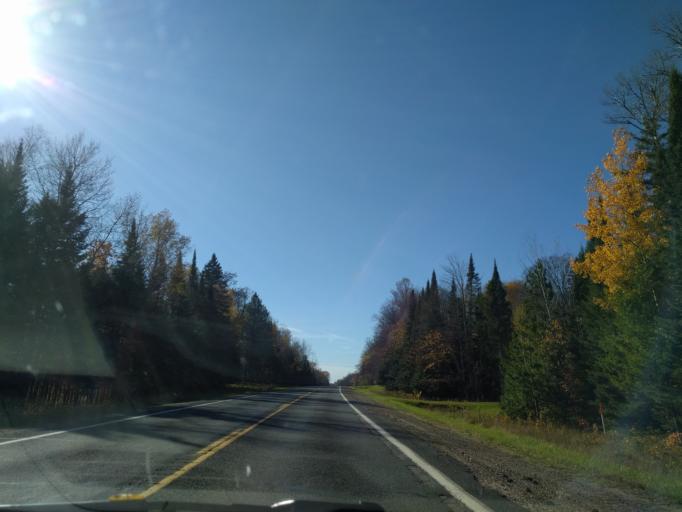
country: US
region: Michigan
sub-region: Iron County
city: Crystal Falls
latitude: 46.1734
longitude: -88.0568
